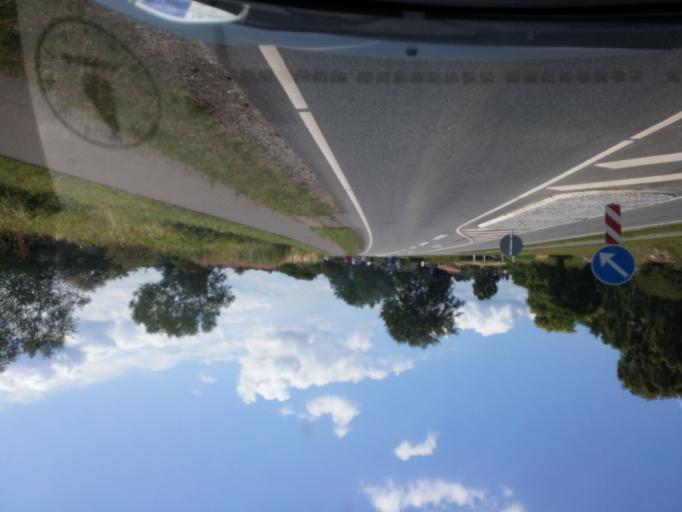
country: DK
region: South Denmark
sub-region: Kerteminde Kommune
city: Munkebo
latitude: 55.4620
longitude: 10.5781
